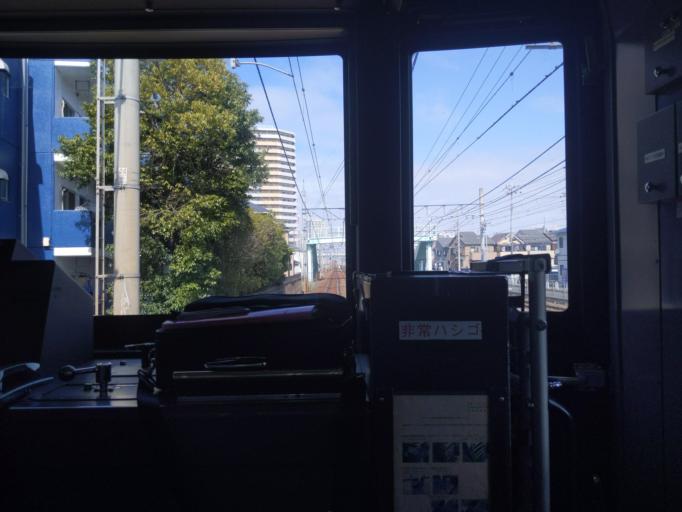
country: JP
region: Saitama
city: Soka
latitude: 35.7839
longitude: 139.7868
